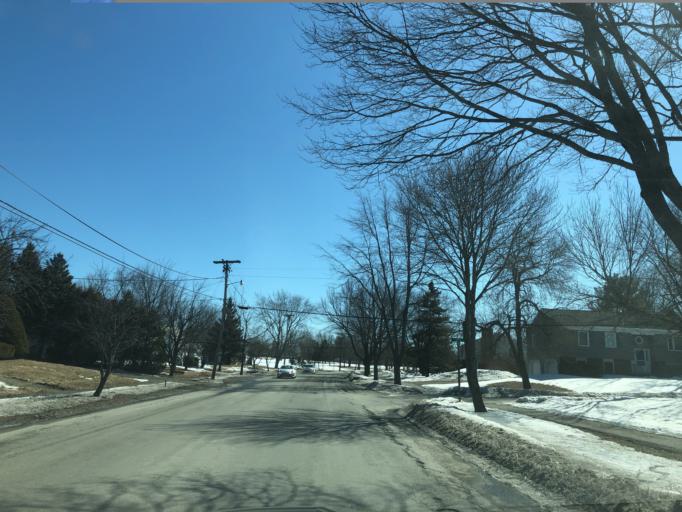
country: US
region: Maine
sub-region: Penobscot County
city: Brewer
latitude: 44.8212
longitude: -68.7608
